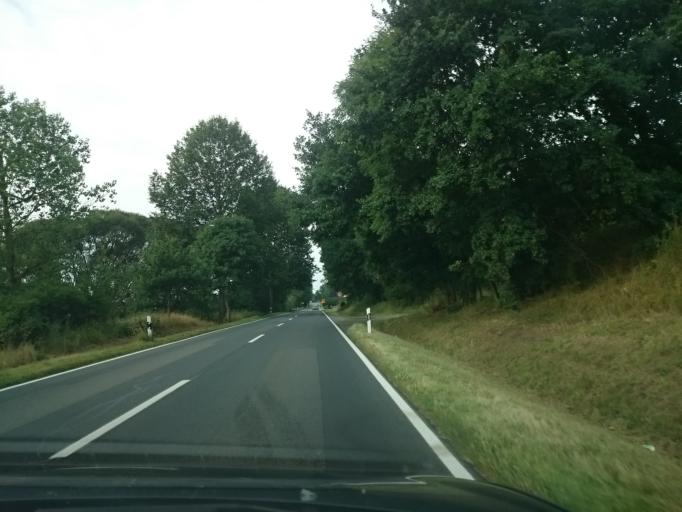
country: DE
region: Mecklenburg-Vorpommern
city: Mollenhagen
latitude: 53.5409
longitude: 12.8365
